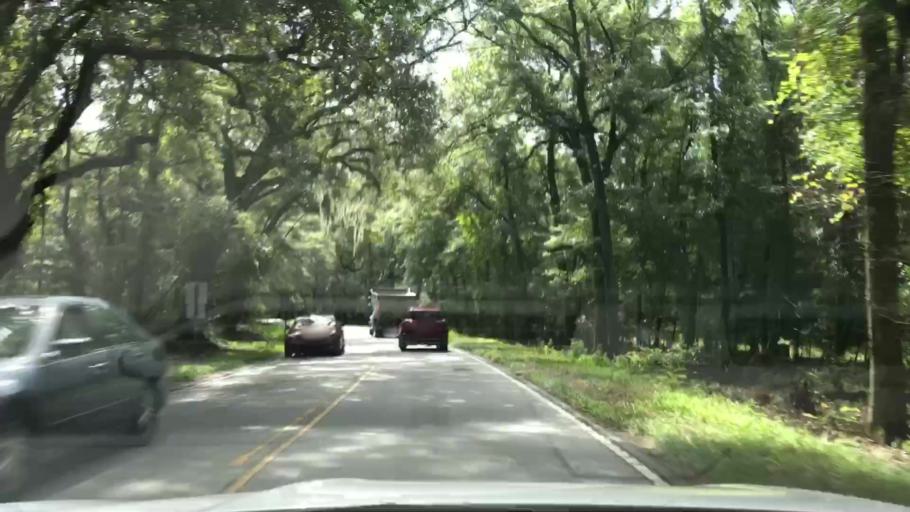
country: US
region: South Carolina
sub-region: Berkeley County
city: Ladson
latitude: 32.8905
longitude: -80.1286
